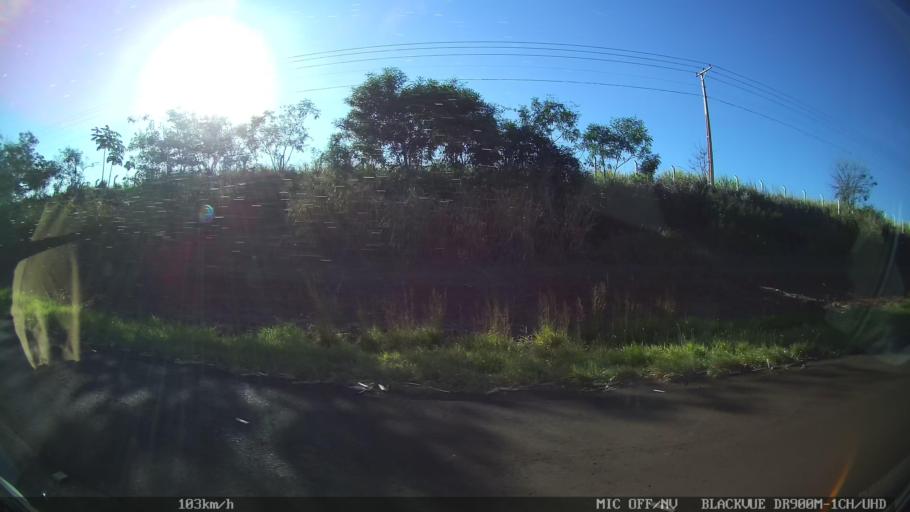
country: BR
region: Sao Paulo
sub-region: Olimpia
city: Olimpia
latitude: -20.7208
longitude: -49.0166
